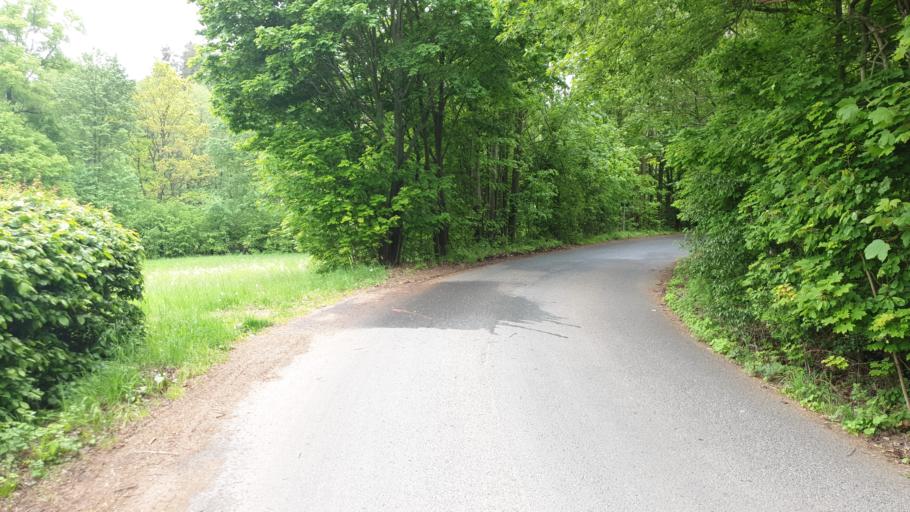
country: DE
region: Saxony
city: Barenstein
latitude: 50.7999
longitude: 13.7758
